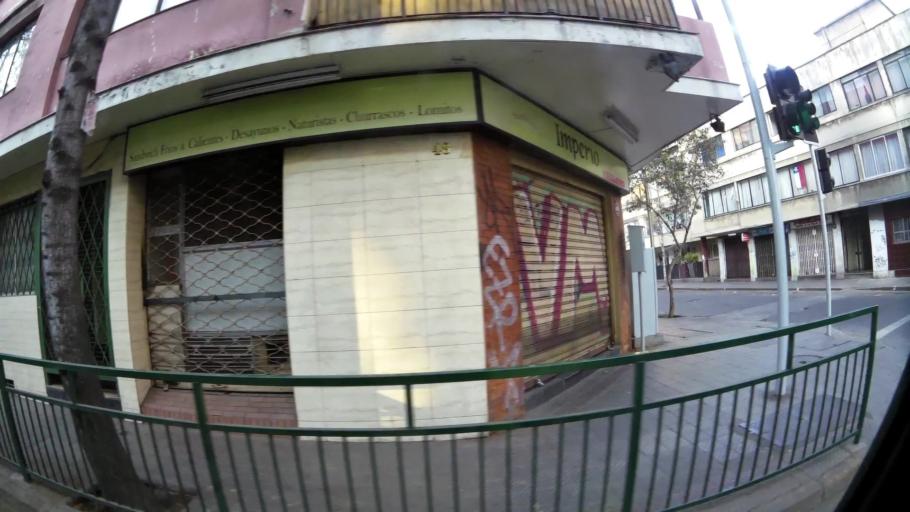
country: CL
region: Santiago Metropolitan
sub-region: Provincia de Santiago
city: Santiago
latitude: -33.4434
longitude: -70.6432
